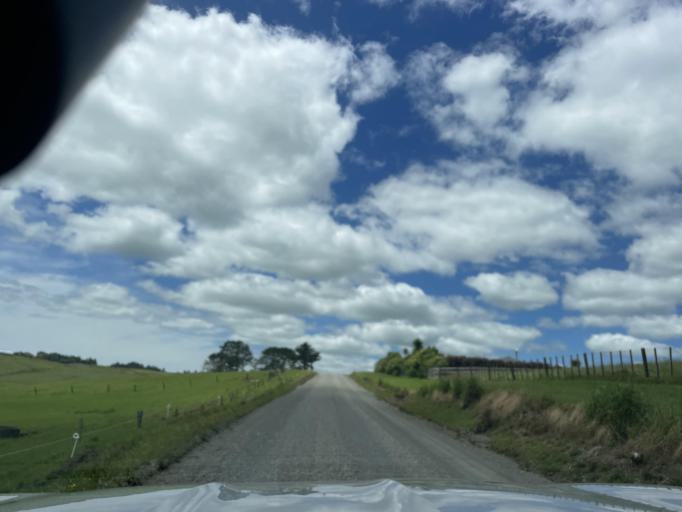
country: NZ
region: Auckland
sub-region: Auckland
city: Wellsford
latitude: -36.1542
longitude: 174.5211
